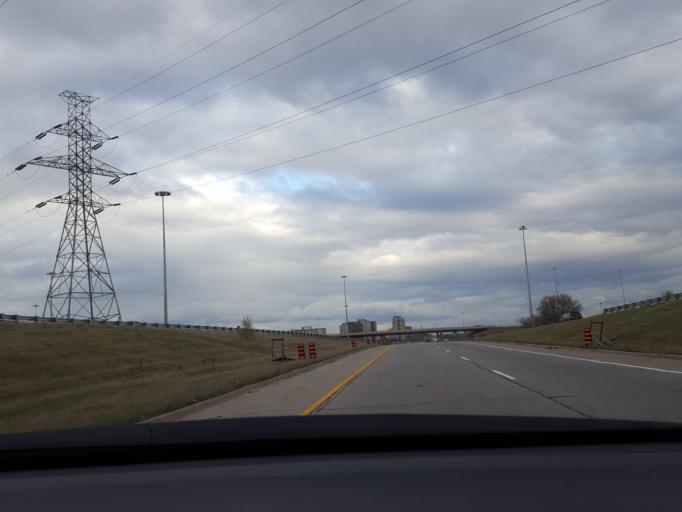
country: CA
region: Ontario
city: Etobicoke
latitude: 43.6710
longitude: -79.5835
